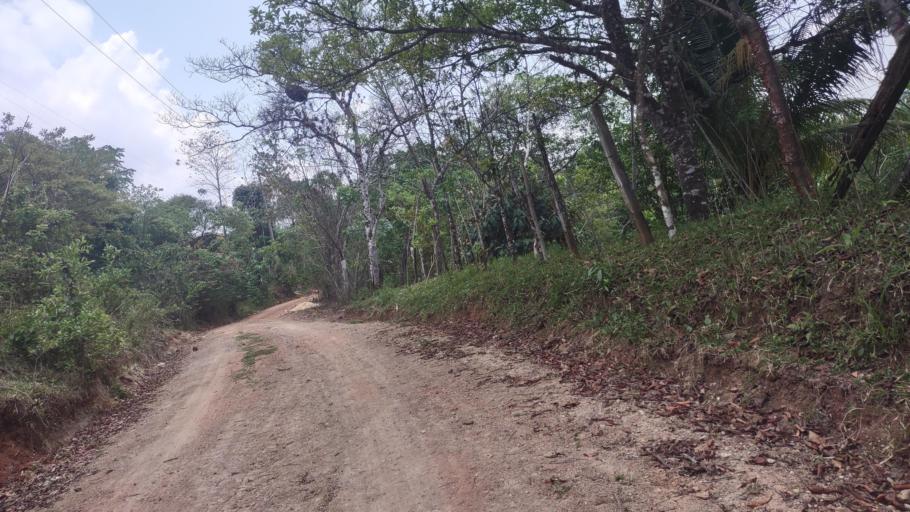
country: MX
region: Tabasco
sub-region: Huimanguillo
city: Francisco Rueda
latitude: 17.6495
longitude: -93.9062
